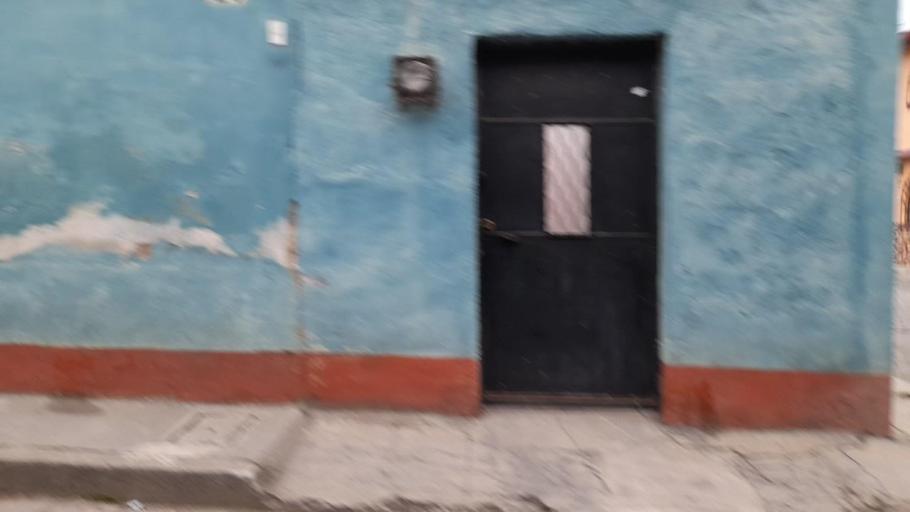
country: GT
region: Quetzaltenango
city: Quetzaltenango
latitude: 14.8316
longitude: -91.5104
